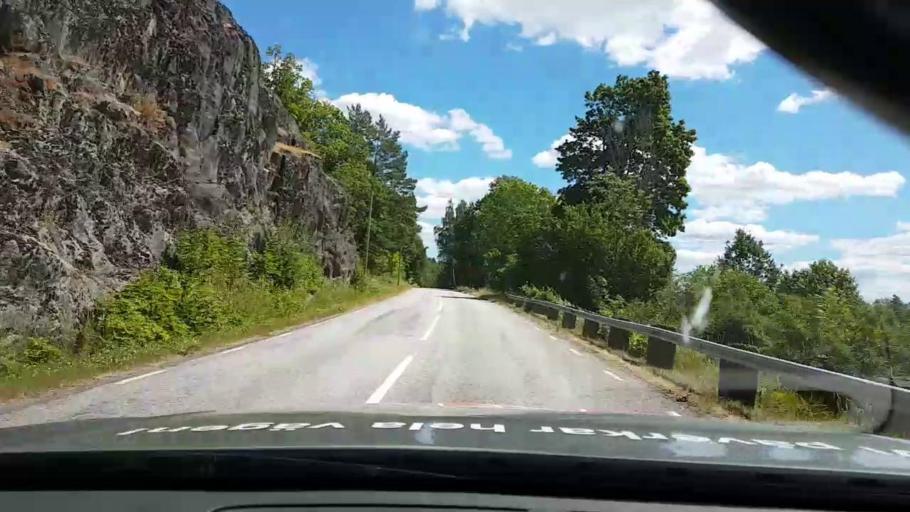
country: SE
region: Kalmar
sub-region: Vasterviks Kommun
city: Overum
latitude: 58.0745
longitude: 16.3648
